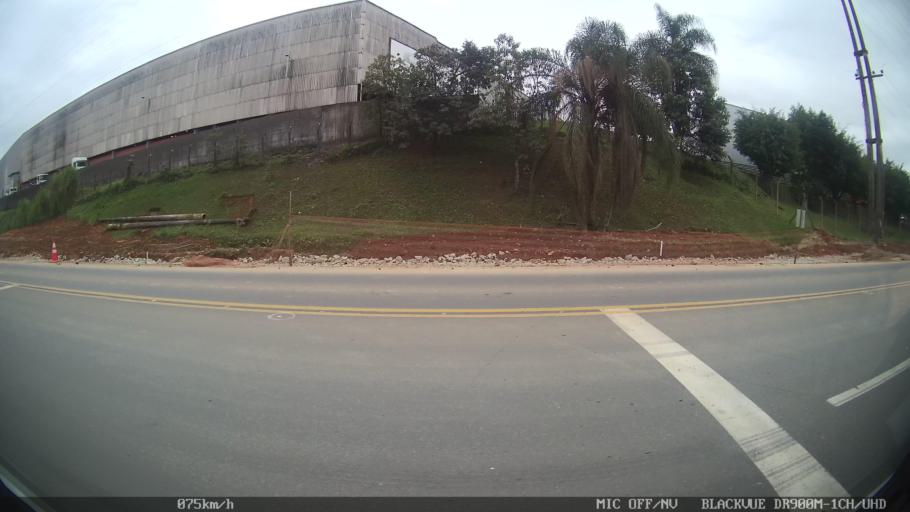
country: BR
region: Santa Catarina
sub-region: Joinville
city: Joinville
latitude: -26.2558
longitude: -48.8758
